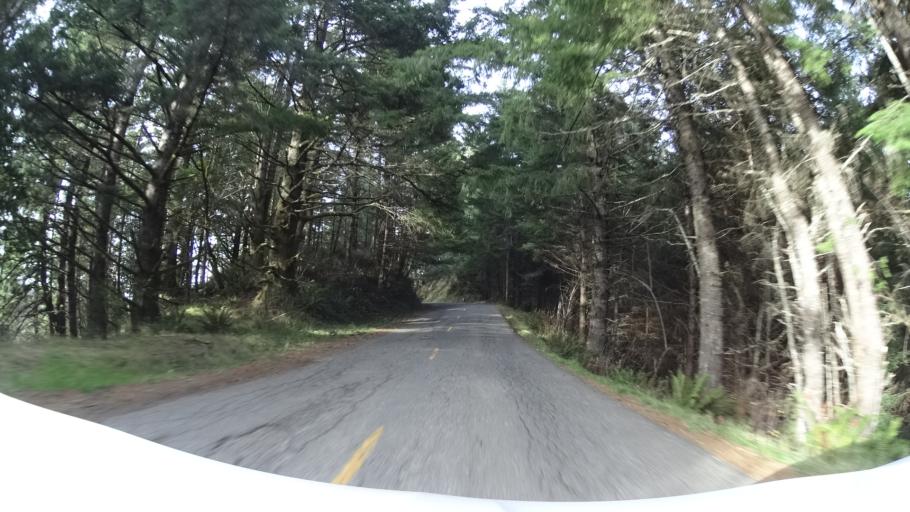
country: US
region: California
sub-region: Humboldt County
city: Ferndale
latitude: 40.5251
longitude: -124.2667
